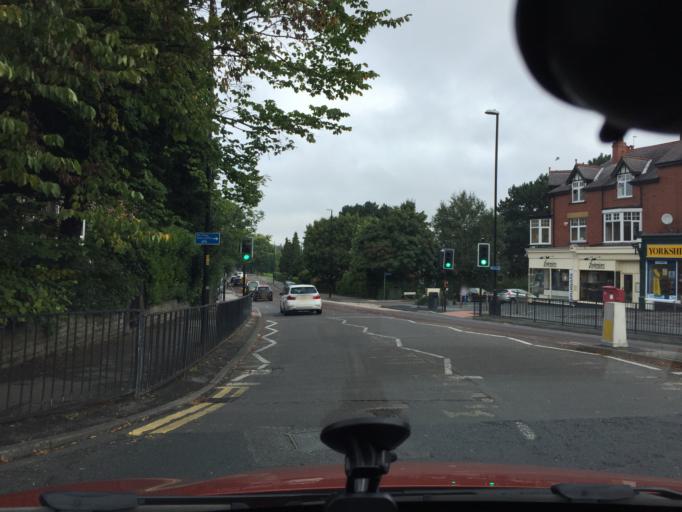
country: GB
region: England
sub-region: North Yorkshire
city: Harrogate
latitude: 53.9827
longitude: -1.5368
